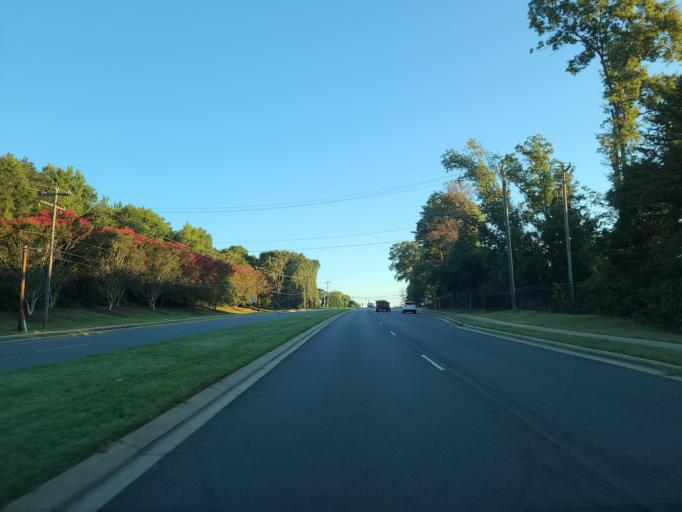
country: US
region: North Carolina
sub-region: Union County
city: Weddington
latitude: 35.0449
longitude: -80.7691
